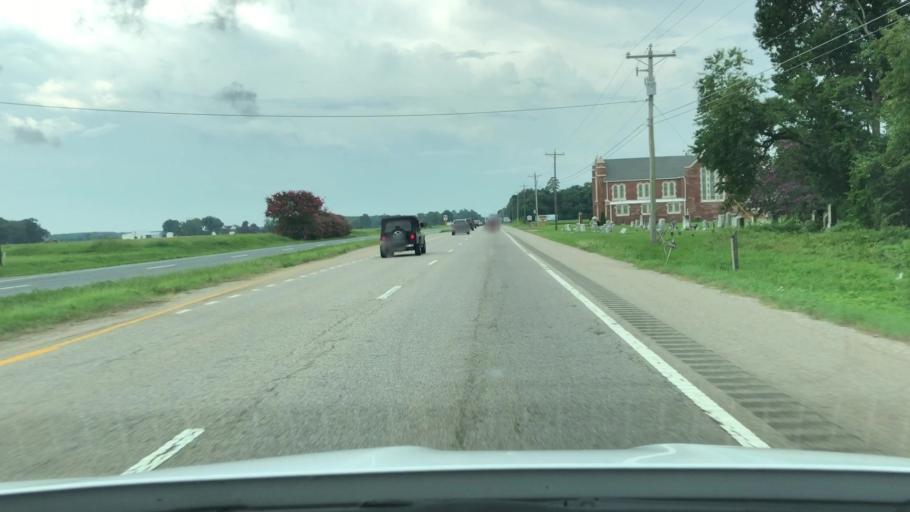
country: US
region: Virginia
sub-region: Northampton County
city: Cape Charles
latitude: 37.2475
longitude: -75.9723
